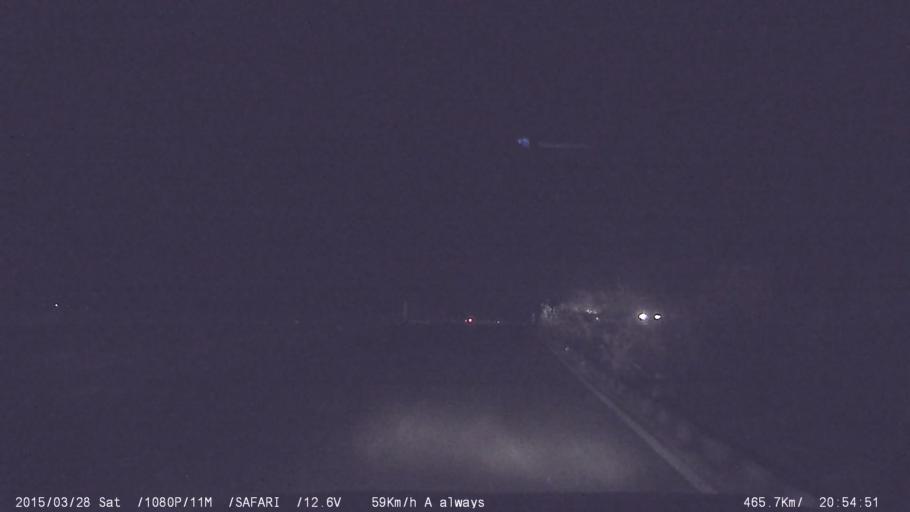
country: IN
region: Karnataka
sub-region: Ramanagara
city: Channapatna
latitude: 12.6825
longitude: 77.2313
